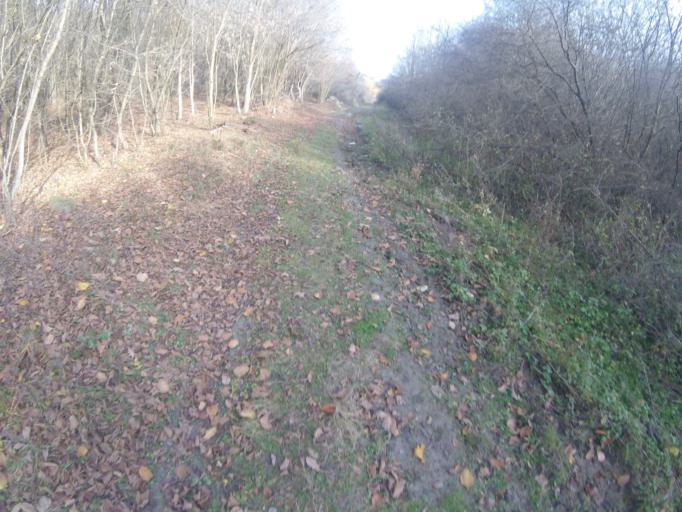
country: HU
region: Borsod-Abauj-Zemplen
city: Sarospatak
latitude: 48.4320
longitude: 21.5179
